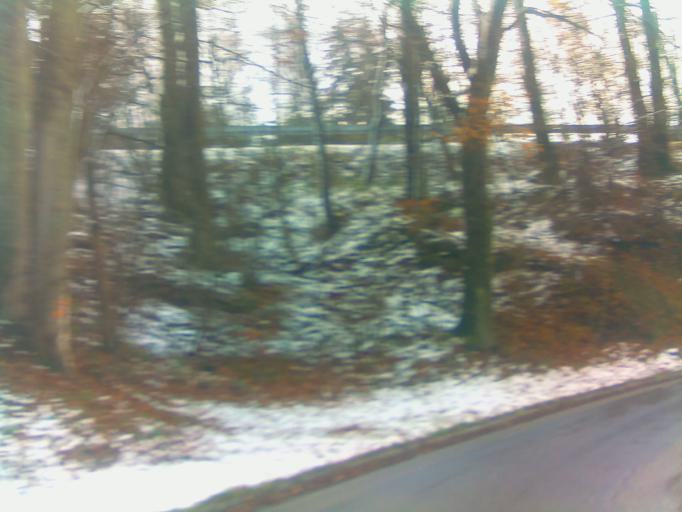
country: DE
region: Hesse
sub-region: Regierungsbezirk Darmstadt
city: Wald-Michelbach
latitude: 49.5637
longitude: 8.8101
